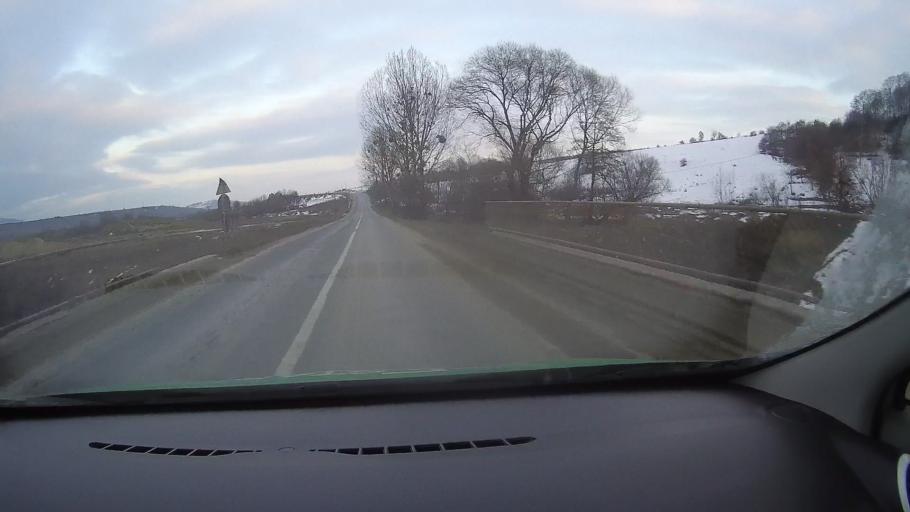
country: RO
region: Harghita
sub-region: Comuna Lupeni
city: Lupeni
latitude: 46.3577
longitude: 25.1983
